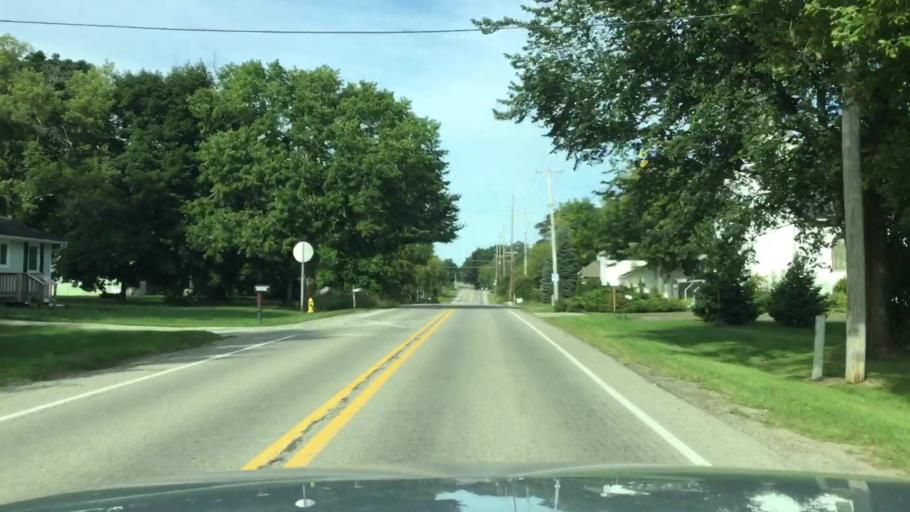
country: US
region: Michigan
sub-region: Genesee County
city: Montrose
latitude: 43.1179
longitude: -83.8874
